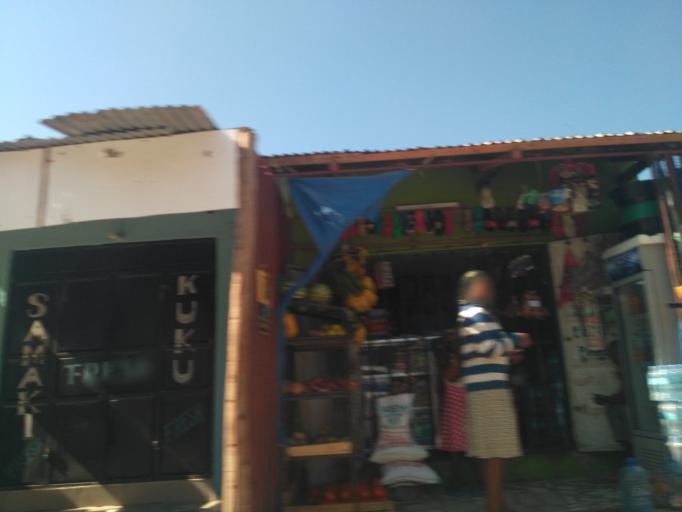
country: TZ
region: Dodoma
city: Dodoma
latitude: -6.1637
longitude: 35.7480
